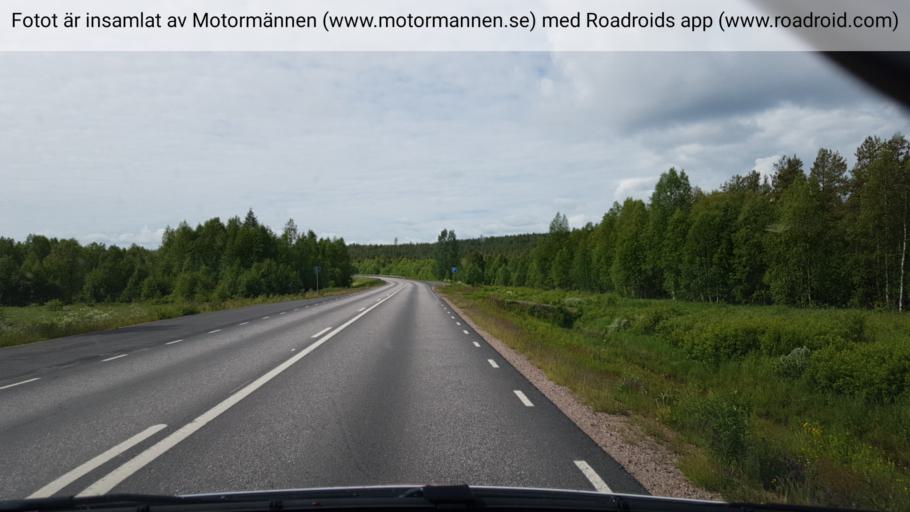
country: SE
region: Norrbotten
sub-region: Overtornea Kommun
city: OEvertornea
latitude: 66.5499
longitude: 23.7959
